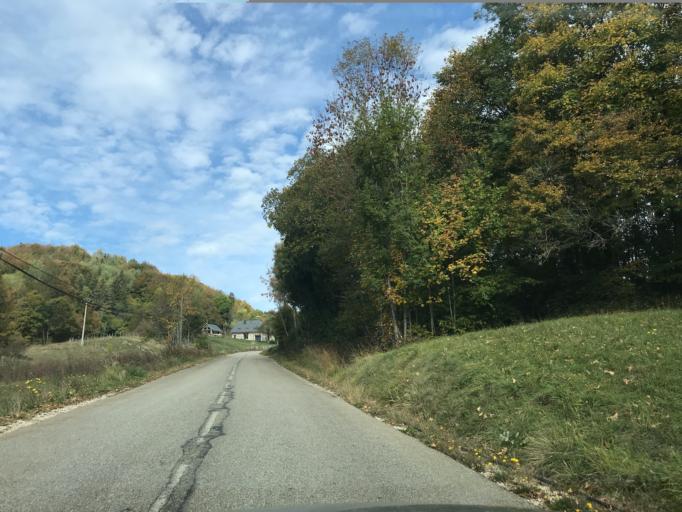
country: FR
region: Rhone-Alpes
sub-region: Departement de la Savoie
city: Les Echelles
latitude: 45.4376
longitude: 5.8097
